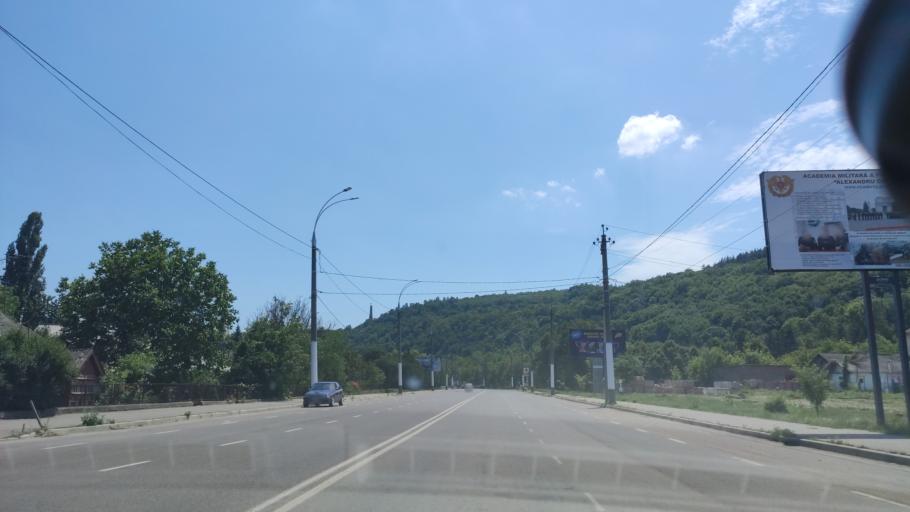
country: MD
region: Raionul Soroca
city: Soroca
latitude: 48.1462
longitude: 28.3021
